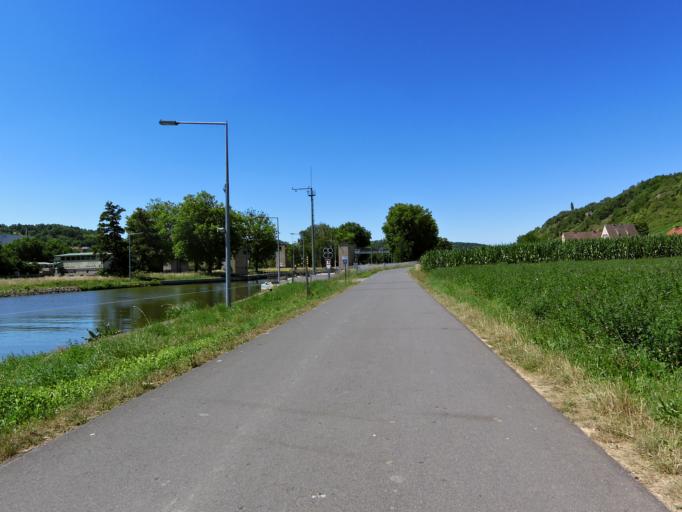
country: DE
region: Bavaria
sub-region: Regierungsbezirk Unterfranken
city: Ochsenfurt
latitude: 49.6760
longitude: 10.0423
